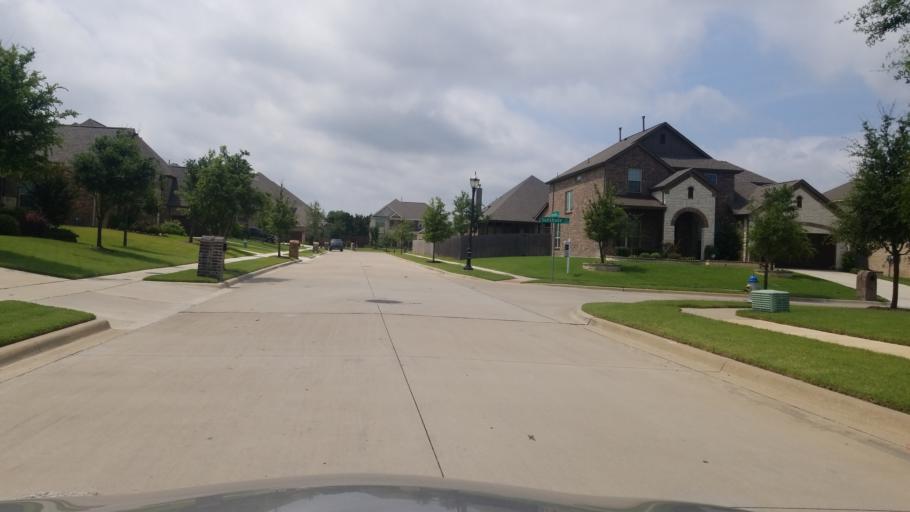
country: US
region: Texas
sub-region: Dallas County
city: Duncanville
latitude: 32.6830
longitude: -96.9355
